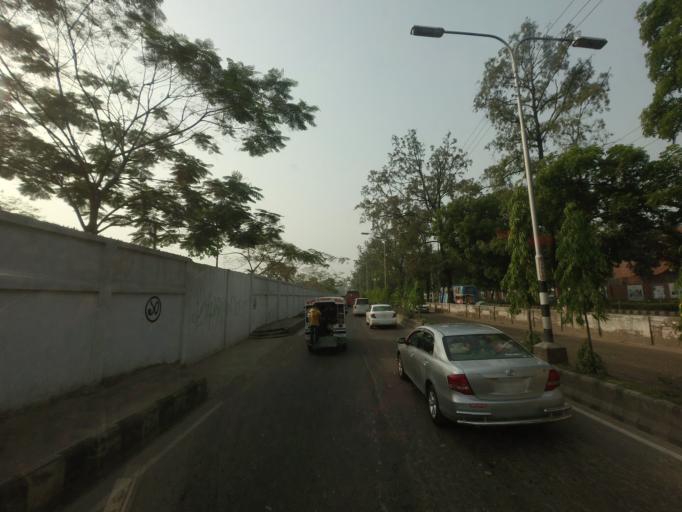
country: BD
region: Dhaka
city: Azimpur
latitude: 23.7733
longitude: 90.3820
